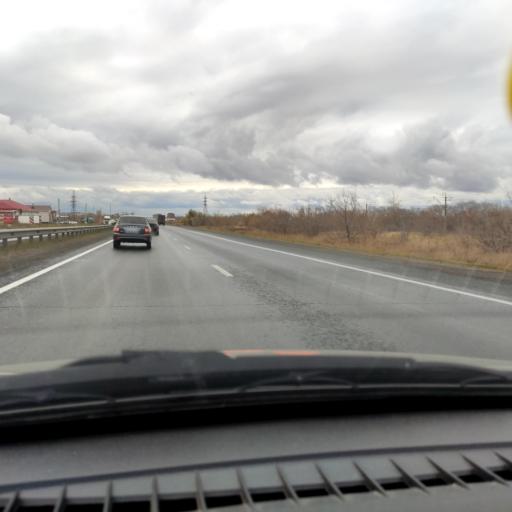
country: RU
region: Samara
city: Tol'yatti
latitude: 53.5652
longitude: 49.3703
